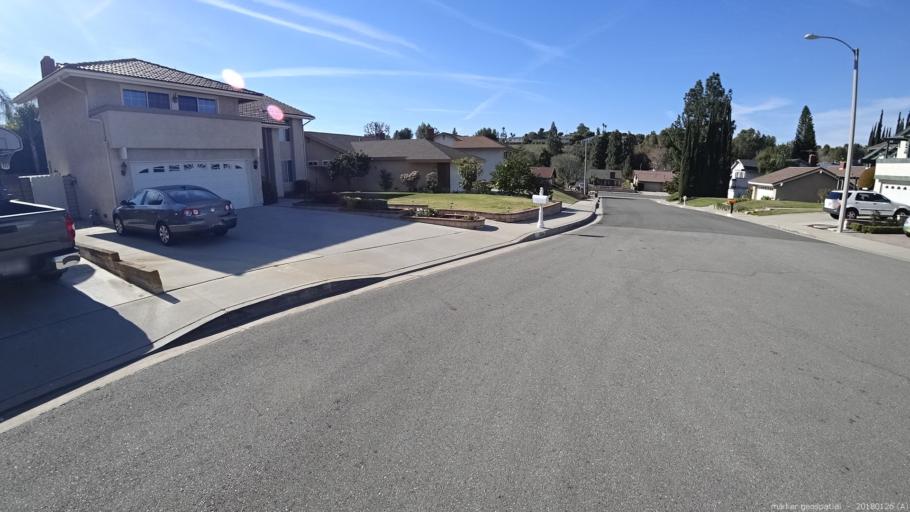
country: US
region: California
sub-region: Los Angeles County
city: Diamond Bar
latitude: 33.9954
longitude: -117.8126
